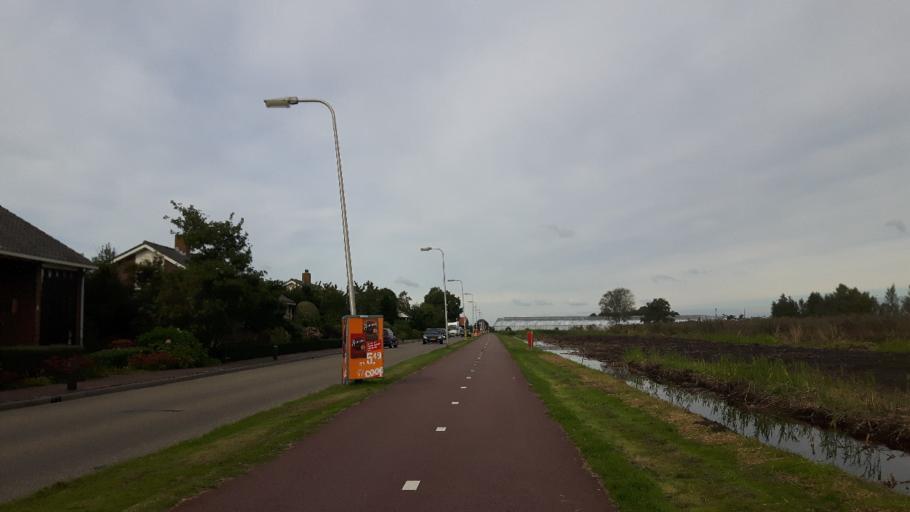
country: NL
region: Utrecht
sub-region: Gemeente De Ronde Venen
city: Mijdrecht
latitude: 52.1671
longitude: 4.8294
